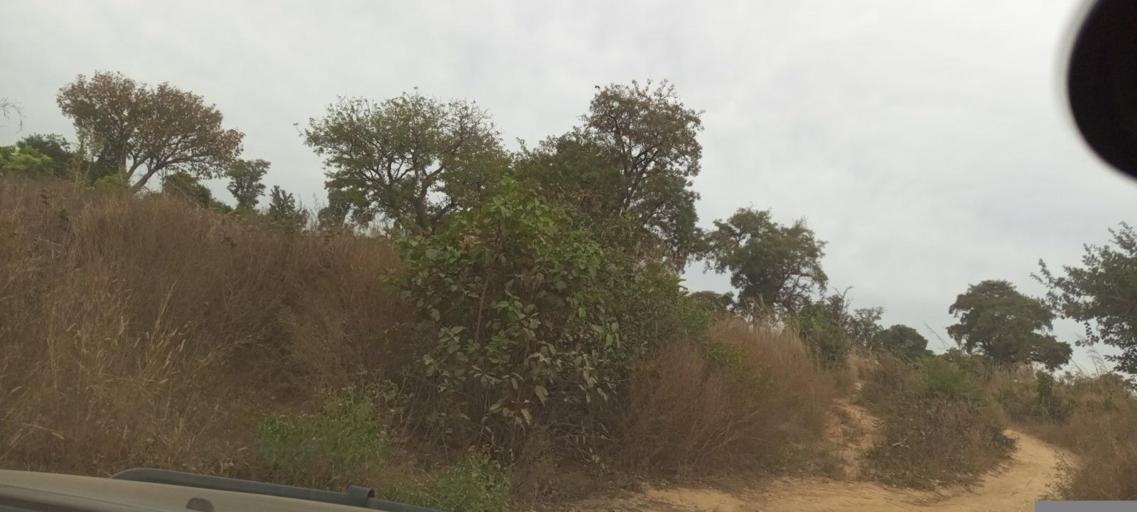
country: ML
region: Koulikoro
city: Kati
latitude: 12.7451
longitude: -8.3550
